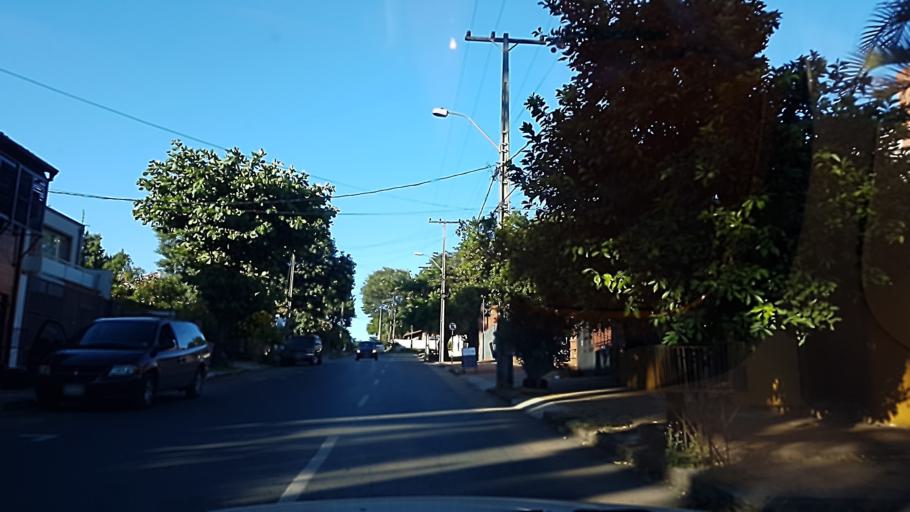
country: PY
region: Asuncion
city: Asuncion
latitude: -25.2698
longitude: -57.5741
